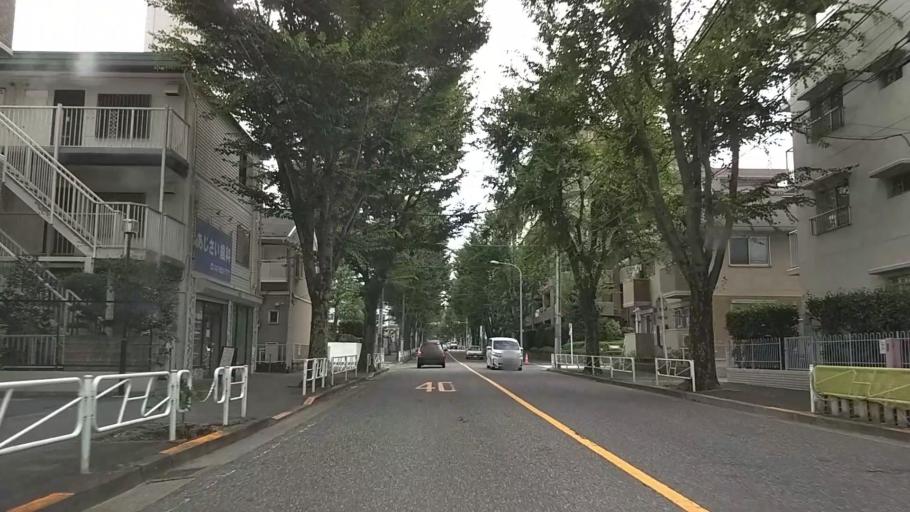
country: JP
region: Tokyo
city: Hachioji
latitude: 35.6482
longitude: 139.3007
